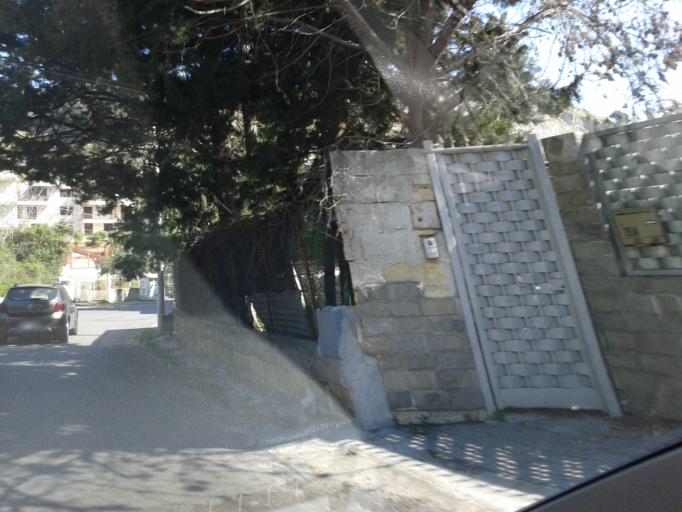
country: IT
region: Sicily
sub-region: Palermo
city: Piano dei Geli
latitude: 38.1174
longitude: 13.2880
